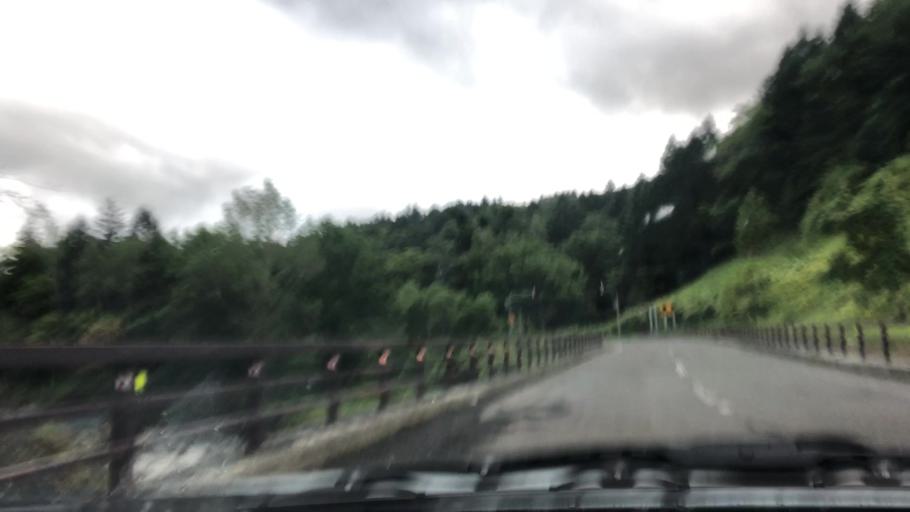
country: JP
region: Hokkaido
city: Shimo-furano
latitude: 42.9360
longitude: 142.3740
